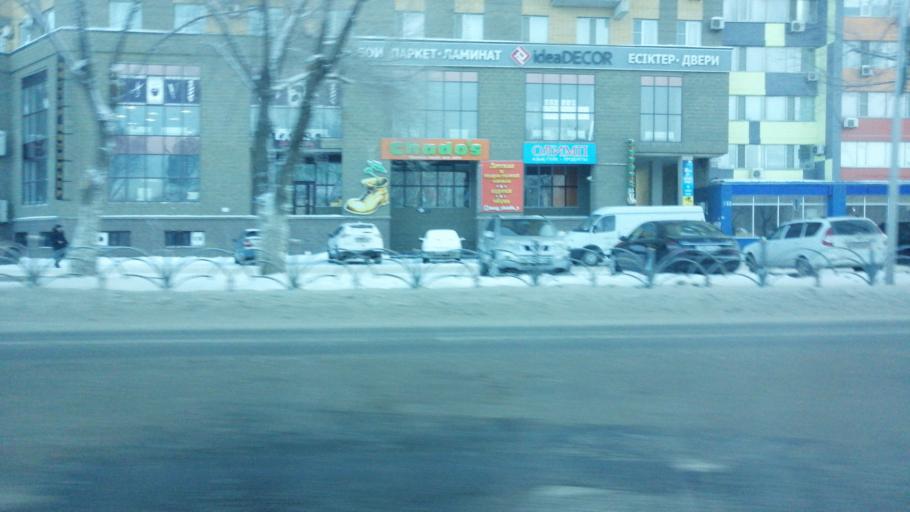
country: KZ
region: Aqtoebe
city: Aqtobe
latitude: 50.2943
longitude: 57.1748
